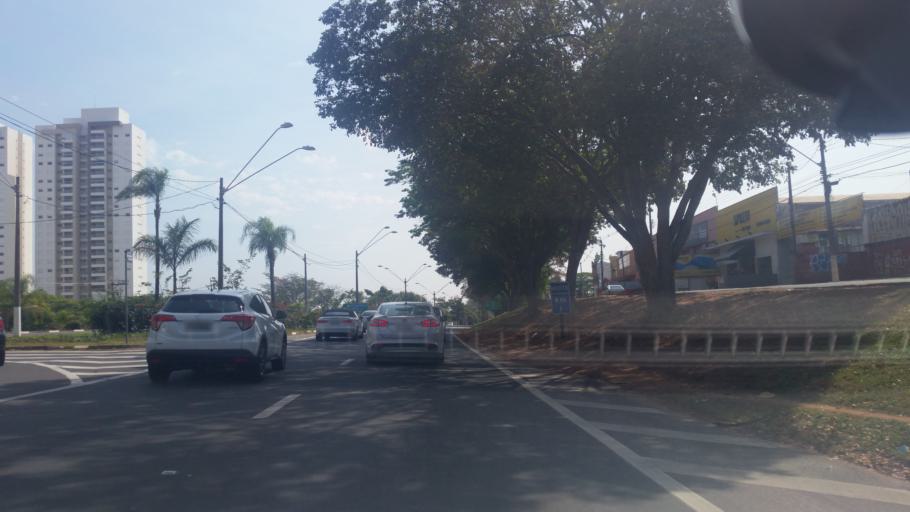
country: BR
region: Sao Paulo
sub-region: Campinas
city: Campinas
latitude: -22.8551
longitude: -47.0440
